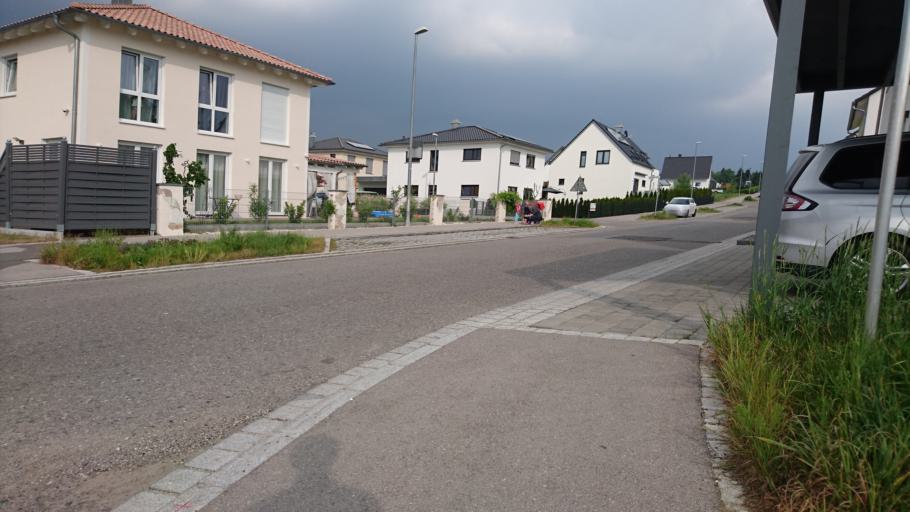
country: DE
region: Bavaria
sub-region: Swabia
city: Diedorf
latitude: 48.3589
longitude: 10.7866
